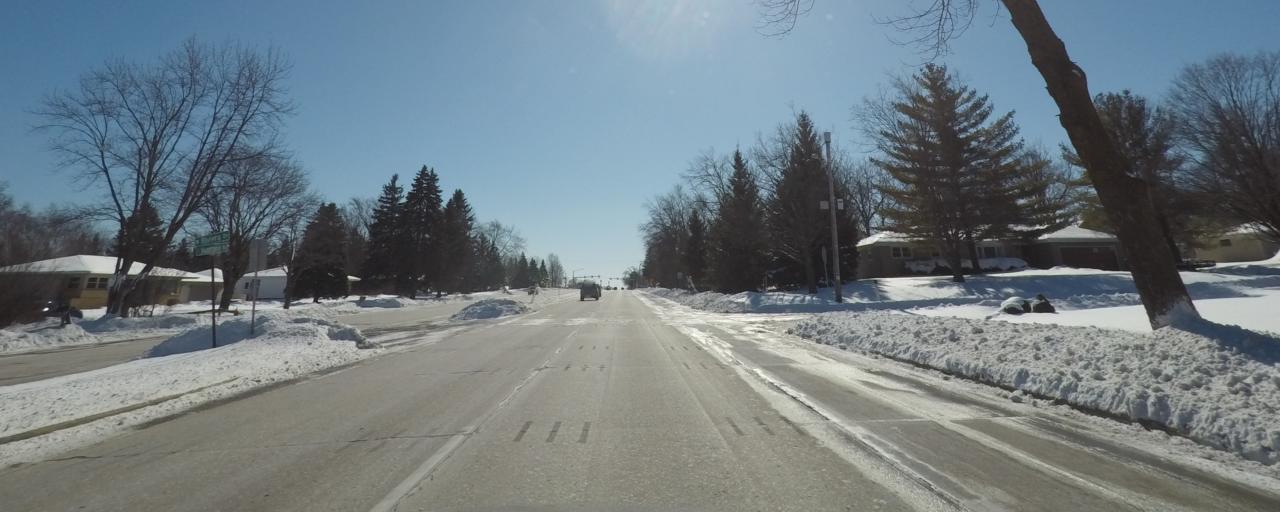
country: US
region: Wisconsin
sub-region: Waukesha County
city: New Berlin
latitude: 42.9843
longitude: -88.1084
